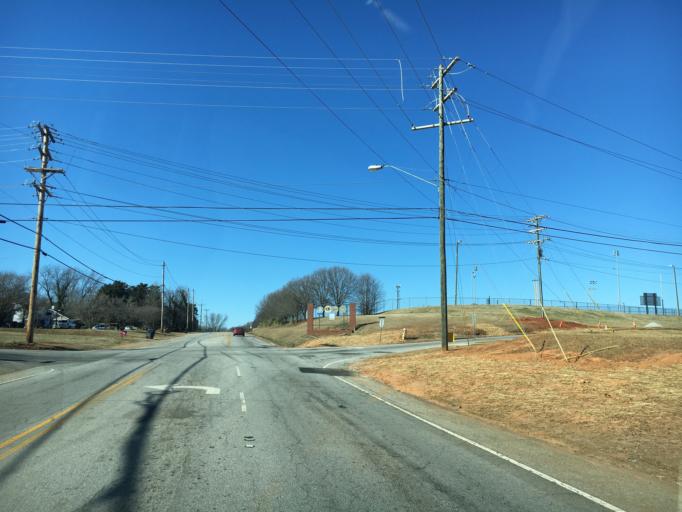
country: US
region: South Carolina
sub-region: Anderson County
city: Anderson
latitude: 34.5076
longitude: -82.6257
